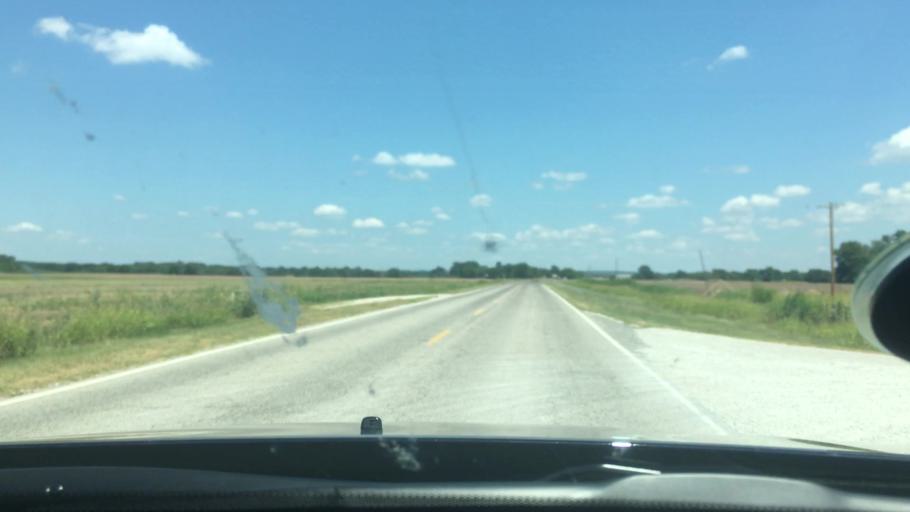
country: US
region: Oklahoma
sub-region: Carter County
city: Dickson
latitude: 34.2226
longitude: -96.9771
